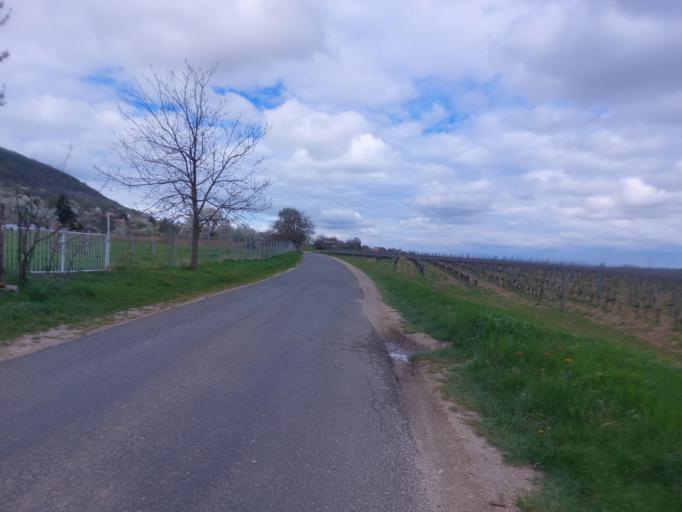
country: HU
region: Veszprem
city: Devecser
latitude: 47.1437
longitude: 17.3895
